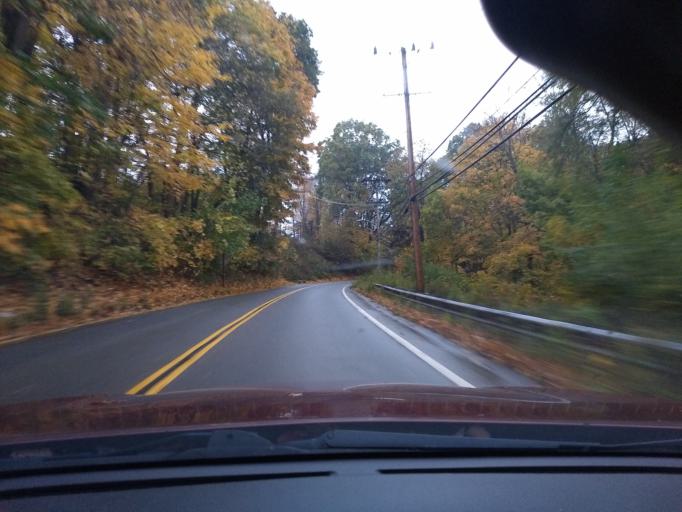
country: US
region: Pennsylvania
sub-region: Allegheny County
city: Jefferson Hills
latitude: 40.2961
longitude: -79.9230
